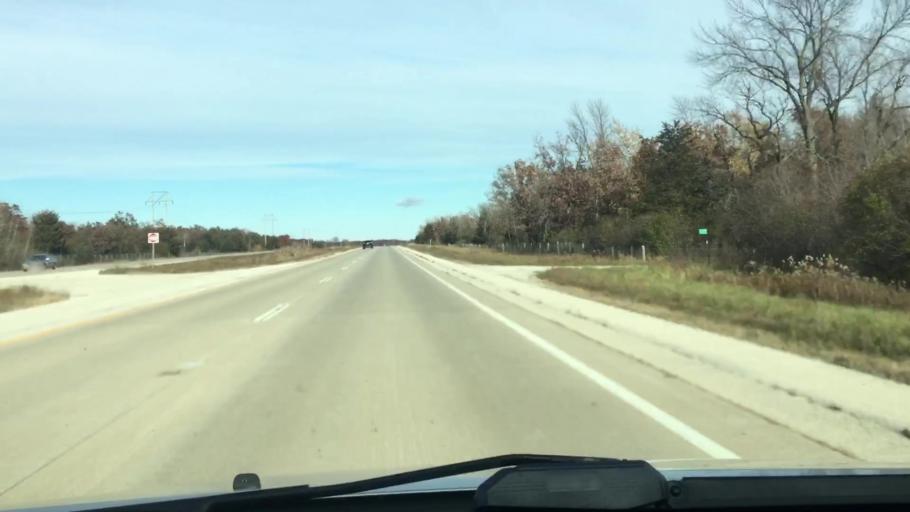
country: US
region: Wisconsin
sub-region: Kewaunee County
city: Luxemburg
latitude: 44.6255
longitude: -87.8176
